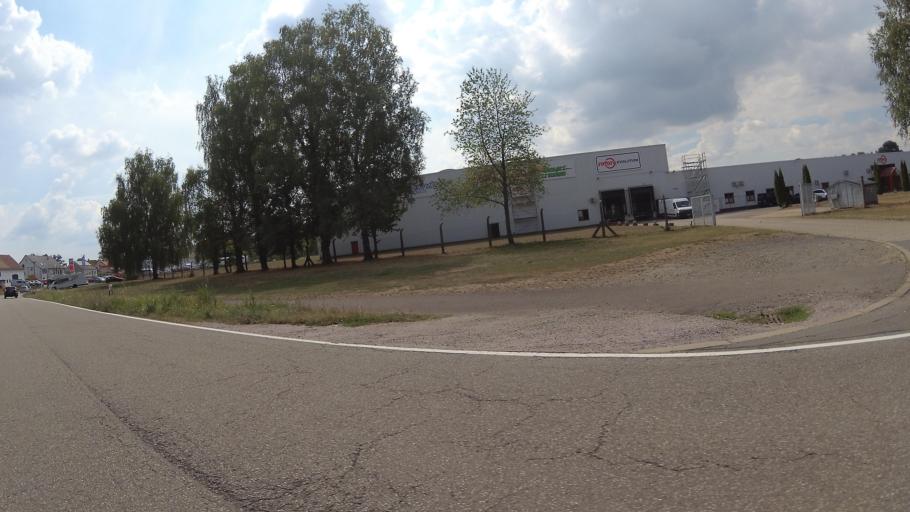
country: DE
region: Rheinland-Pfalz
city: Hornbach
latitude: 49.1904
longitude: 7.3689
